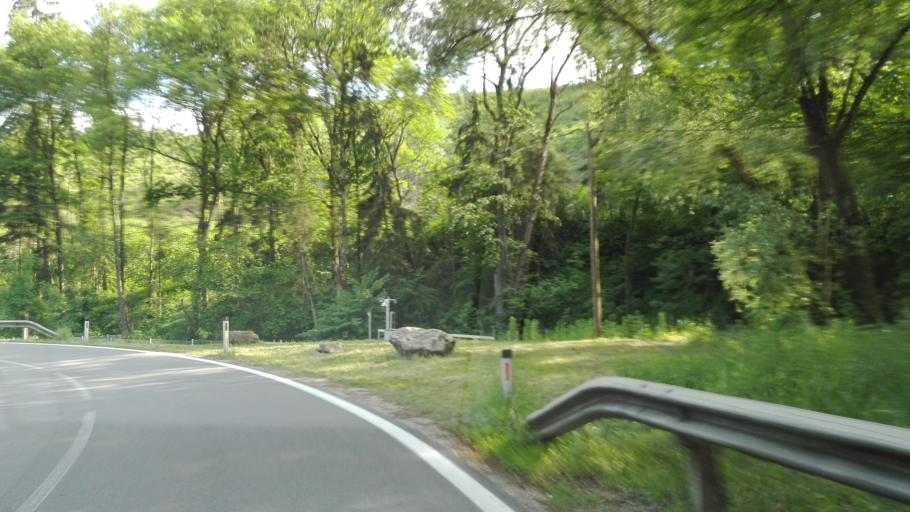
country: AT
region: Upper Austria
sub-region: Politischer Bezirk Urfahr-Umgebung
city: Engerwitzdorf
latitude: 48.3400
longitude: 14.4578
